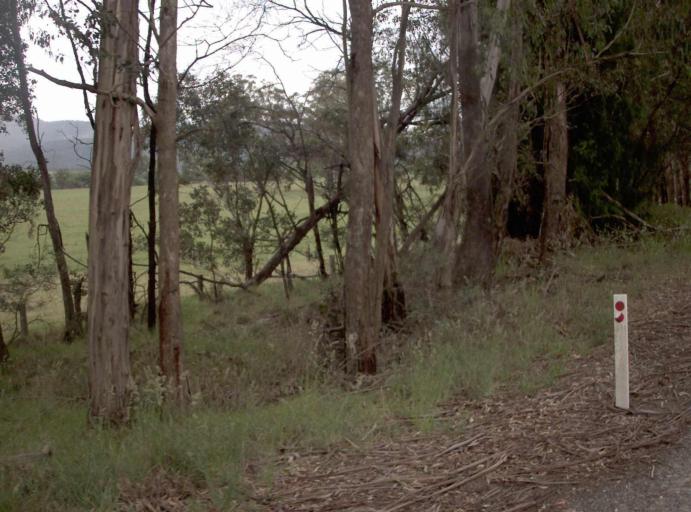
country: AU
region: New South Wales
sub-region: Bombala
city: Bombala
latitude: -37.5078
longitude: 149.1741
